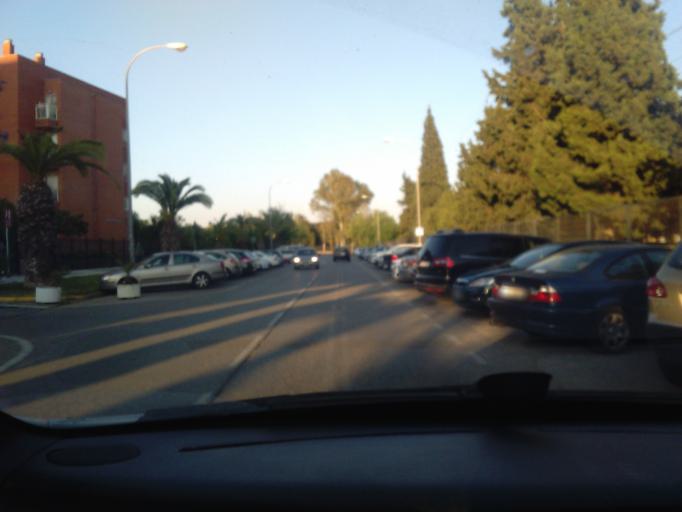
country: ES
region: Andalusia
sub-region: Provincia de Sevilla
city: Sevilla
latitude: 37.3971
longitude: -5.9421
